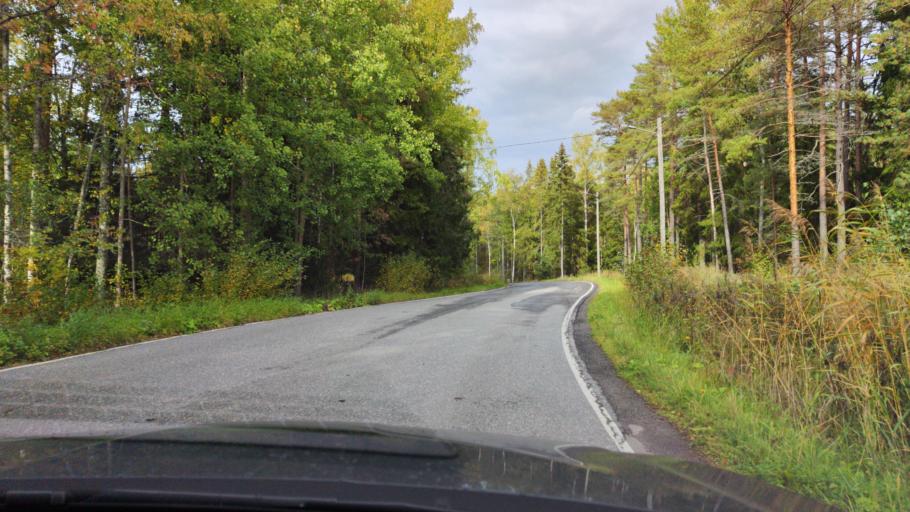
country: FI
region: Varsinais-Suomi
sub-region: Aboland-Turunmaa
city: Pargas
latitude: 60.3485
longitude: 22.1847
